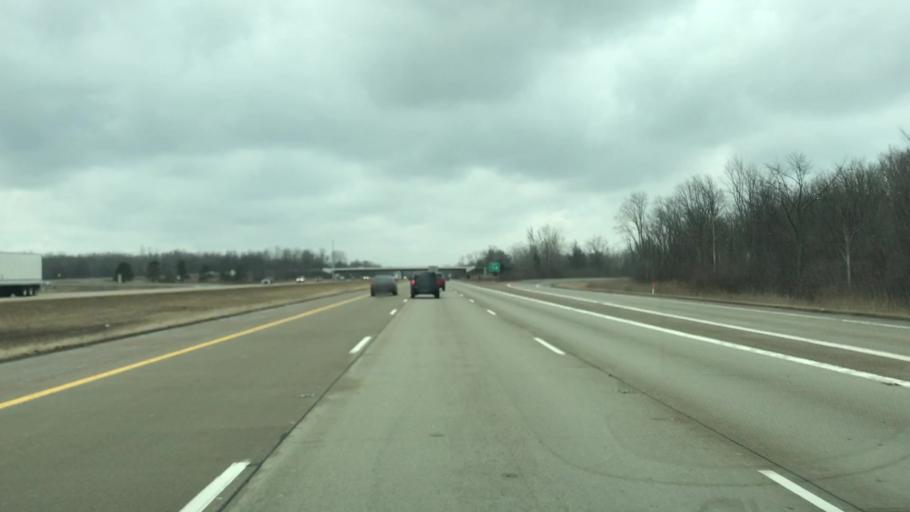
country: US
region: Michigan
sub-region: Monroe County
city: Carleton
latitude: 42.1317
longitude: -83.3815
